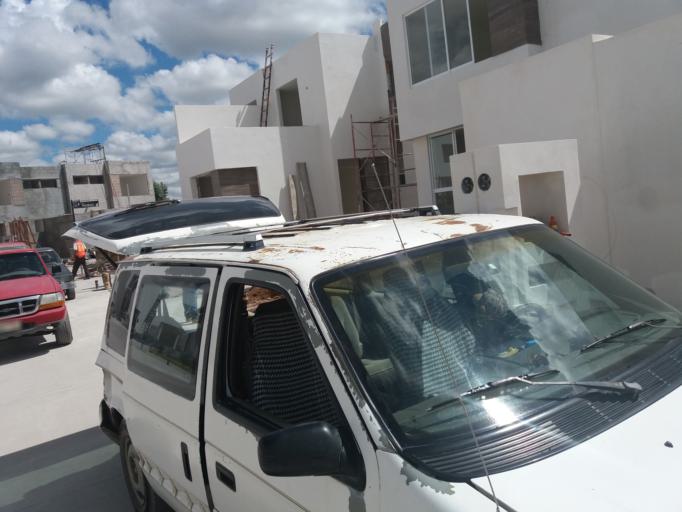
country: MX
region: Aguascalientes
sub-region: Aguascalientes
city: San Sebastian [Fraccionamiento]
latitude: 21.8193
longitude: -102.2740
